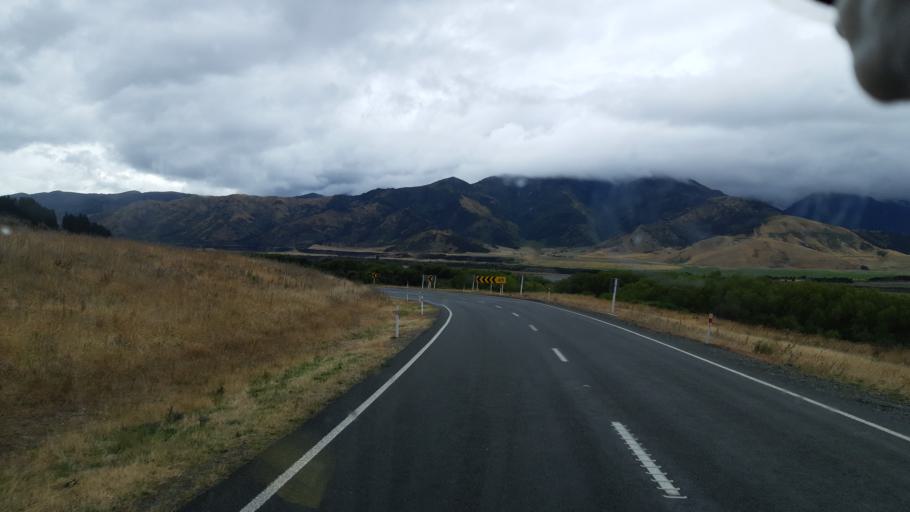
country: NZ
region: Canterbury
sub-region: Hurunui District
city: Amberley
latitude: -42.5716
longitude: 172.7103
